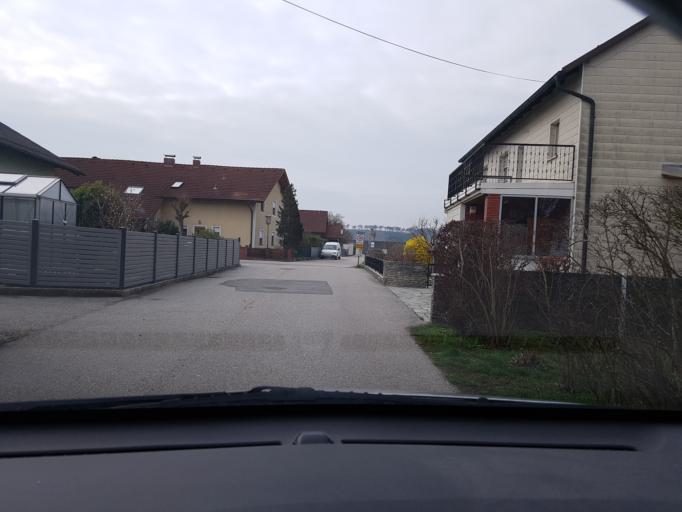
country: AT
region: Upper Austria
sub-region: Politischer Bezirk Linz-Land
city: Asten
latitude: 48.2169
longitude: 14.4164
